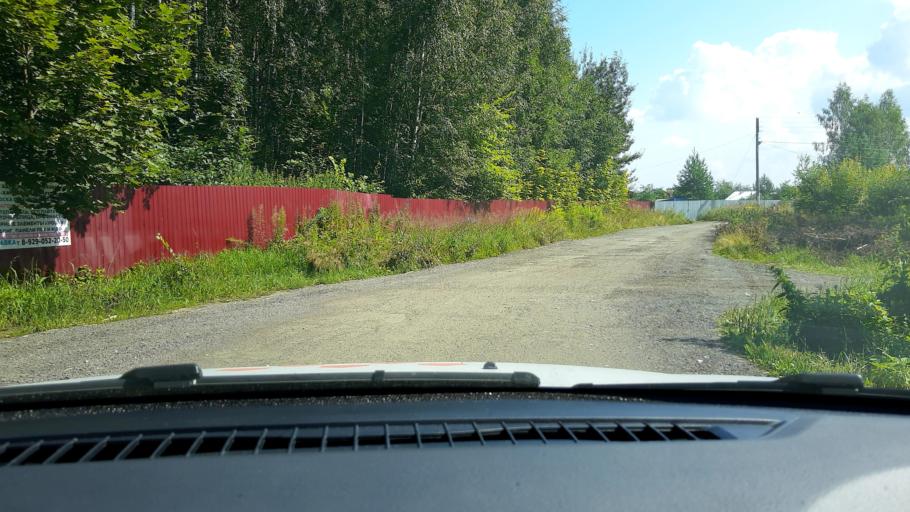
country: RU
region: Nizjnij Novgorod
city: Kstovo
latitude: 56.0545
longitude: 43.9954
